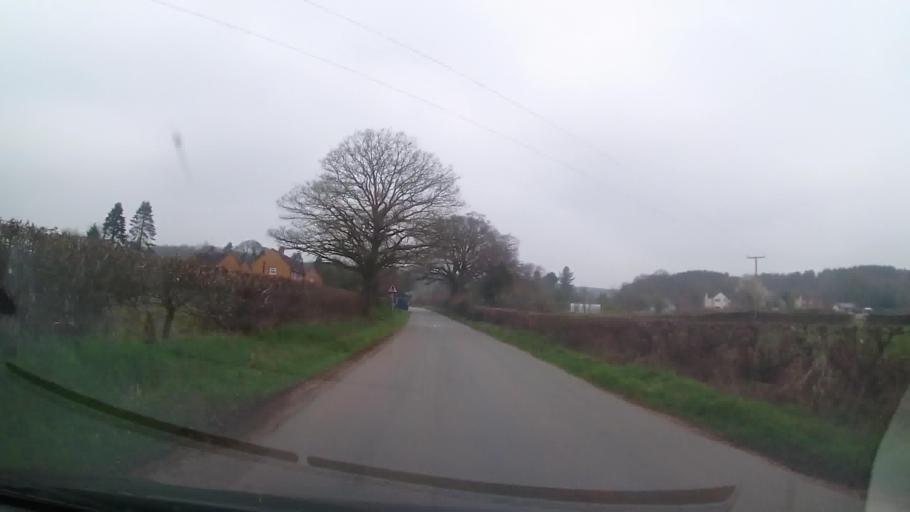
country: GB
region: England
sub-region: Staffordshire
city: Standon
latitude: 52.9458
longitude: -2.3517
